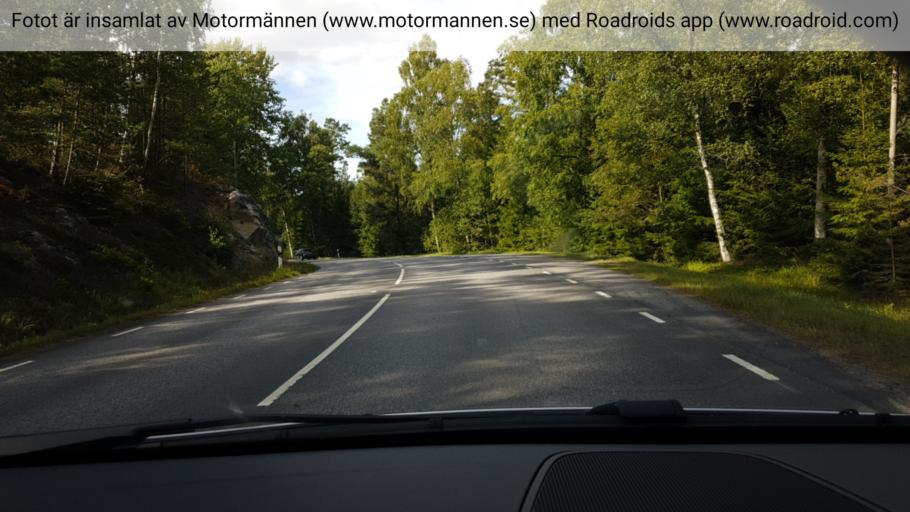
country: SE
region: Stockholm
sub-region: Sodertalje Kommun
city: Pershagen
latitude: 59.1262
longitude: 17.6546
